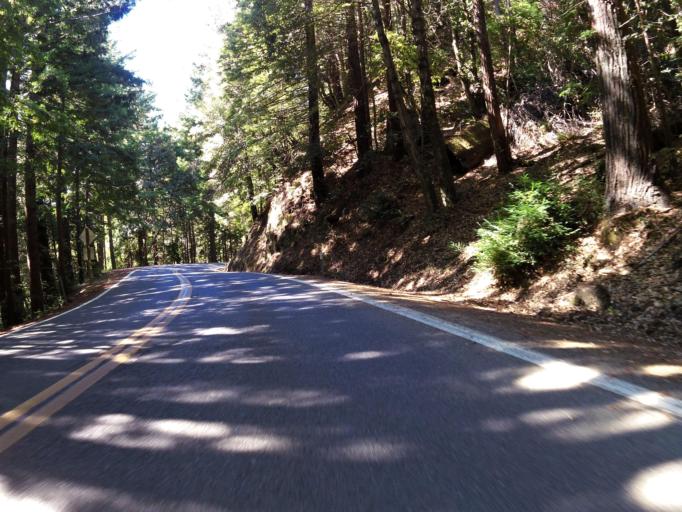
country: US
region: California
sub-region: Humboldt County
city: Redway
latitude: 39.7971
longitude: -123.8097
